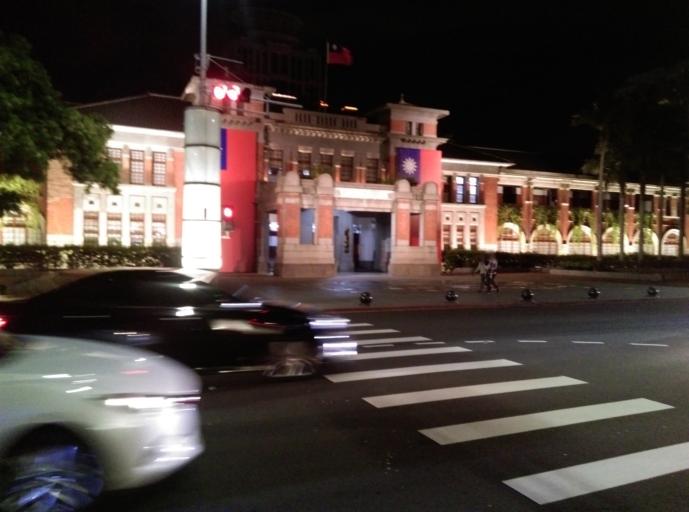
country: TW
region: Taiwan
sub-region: Hsinchu
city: Hsinchu
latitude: 24.8067
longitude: 120.9685
